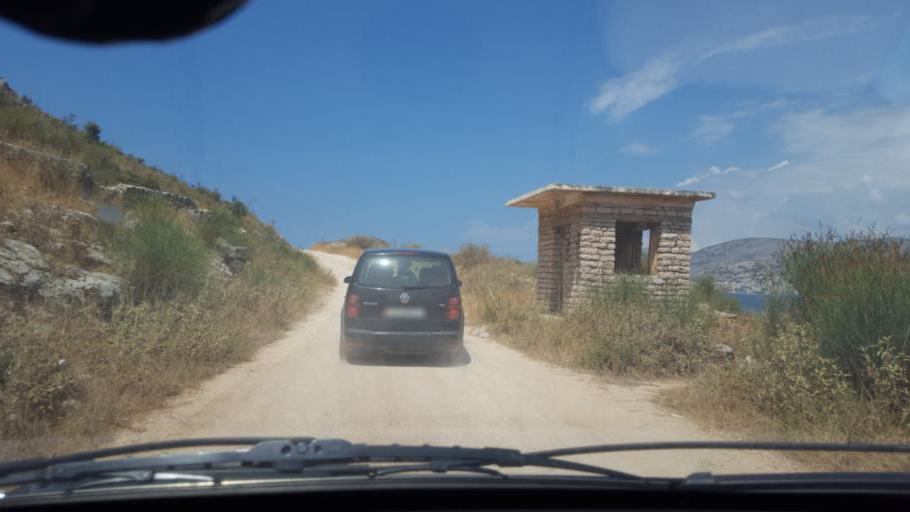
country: AL
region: Vlore
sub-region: Rrethi i Sarandes
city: Sarande
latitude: 39.8421
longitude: 20.0206
